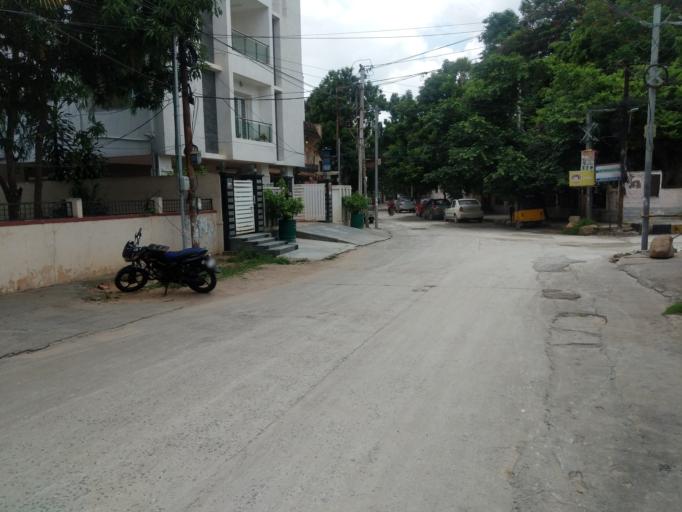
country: IN
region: Telangana
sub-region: Rangareddi
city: Kukatpalli
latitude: 17.4408
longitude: 78.4358
